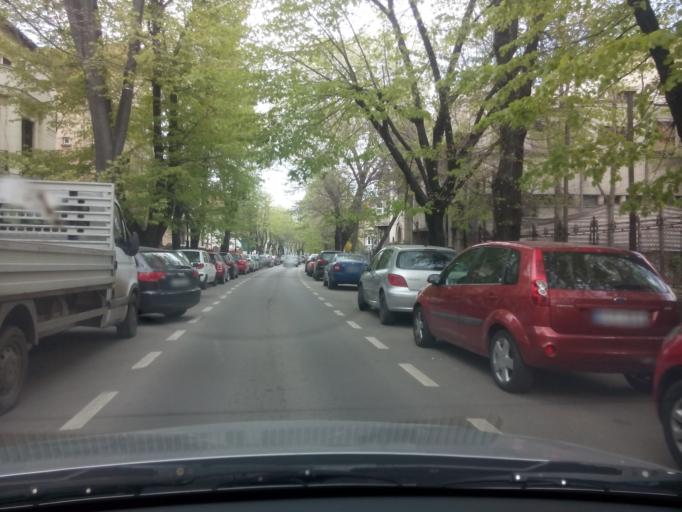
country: RO
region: Bucuresti
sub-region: Municipiul Bucuresti
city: Bucharest
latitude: 44.4561
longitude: 26.0941
